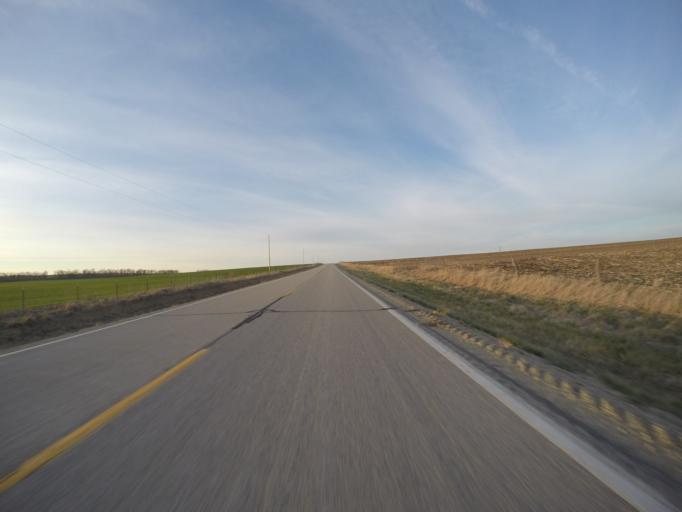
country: US
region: Kansas
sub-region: Clay County
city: Clay Center
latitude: 39.3869
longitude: -96.8493
